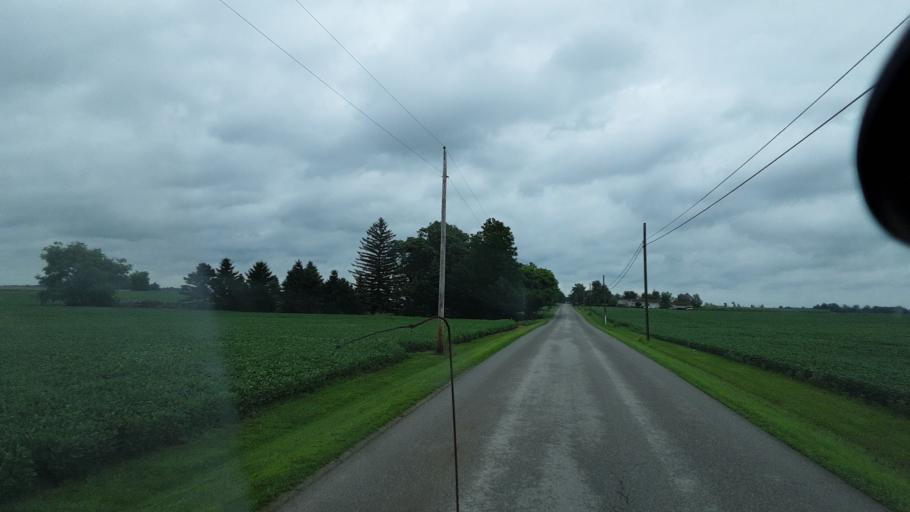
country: US
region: Indiana
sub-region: Adams County
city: Geneva
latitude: 40.5335
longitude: -84.9856
